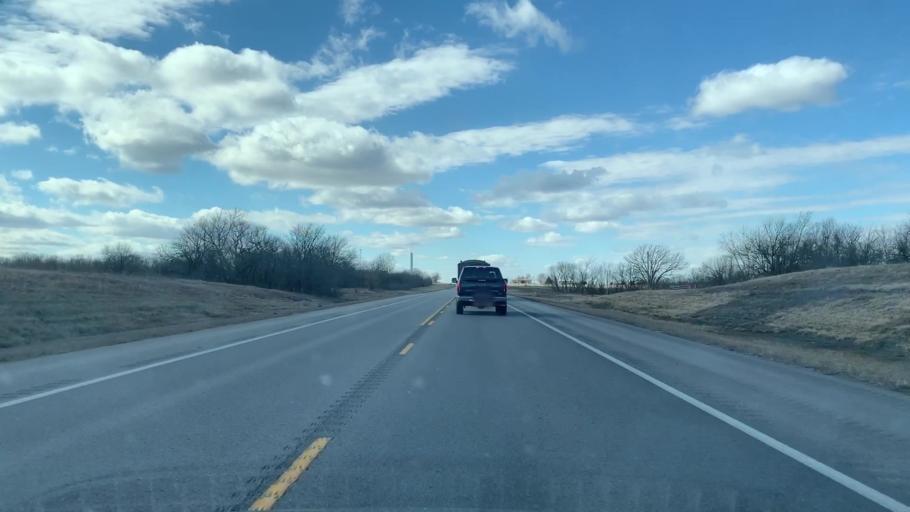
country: US
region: Kansas
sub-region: Cherokee County
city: Columbus
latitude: 37.3400
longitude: -94.8974
